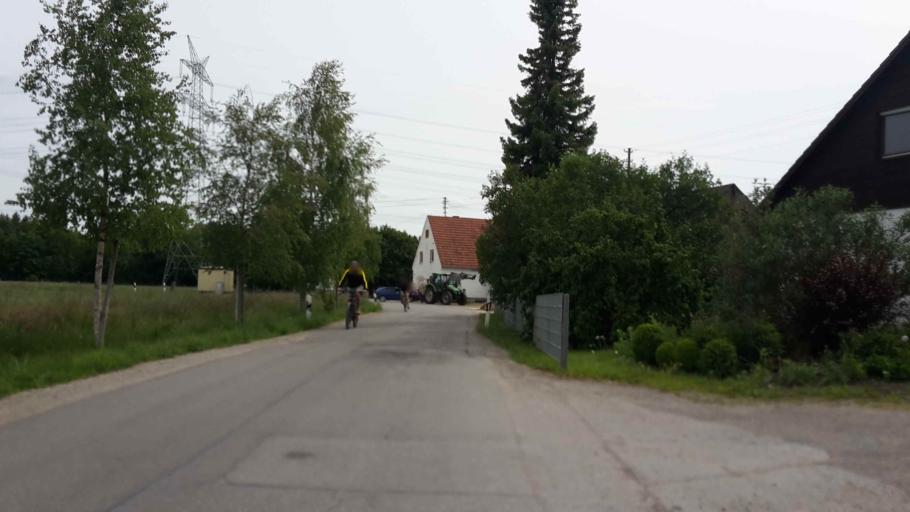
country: DE
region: Bavaria
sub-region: Upper Bavaria
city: Dachau
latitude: 48.2208
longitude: 11.4231
